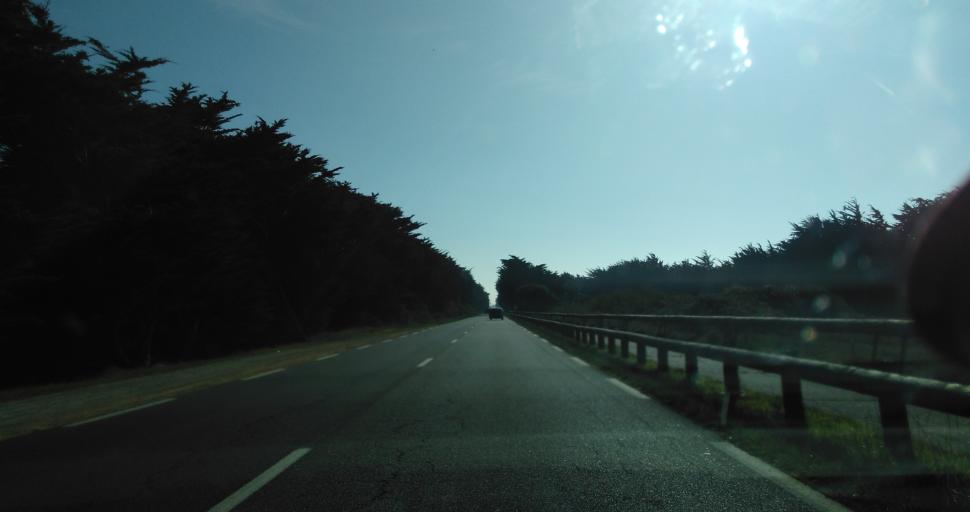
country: FR
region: Brittany
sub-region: Departement du Morbihan
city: Plouharnel
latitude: 47.5683
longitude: -3.1346
